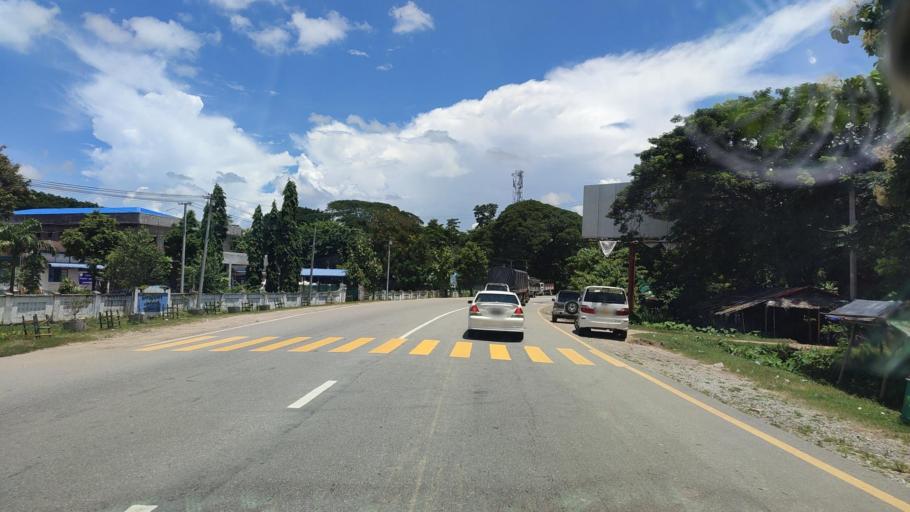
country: MM
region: Bago
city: Nyaunglebin
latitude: 18.1598
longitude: 96.6092
